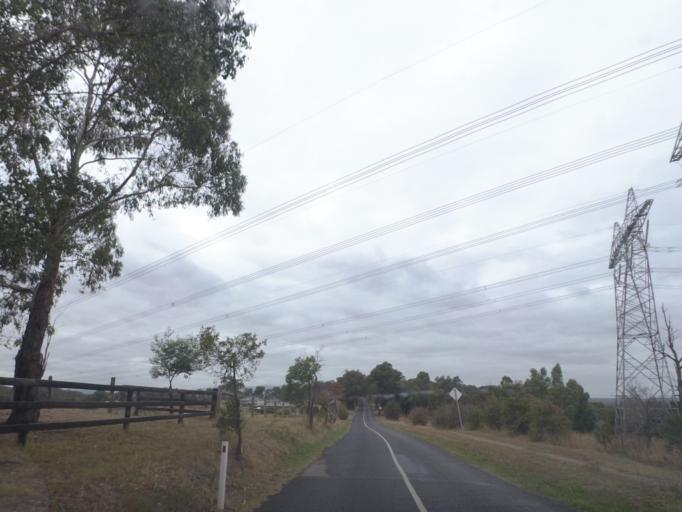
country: AU
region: Victoria
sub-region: Nillumbik
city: North Warrandyte
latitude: -37.6930
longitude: 145.2343
